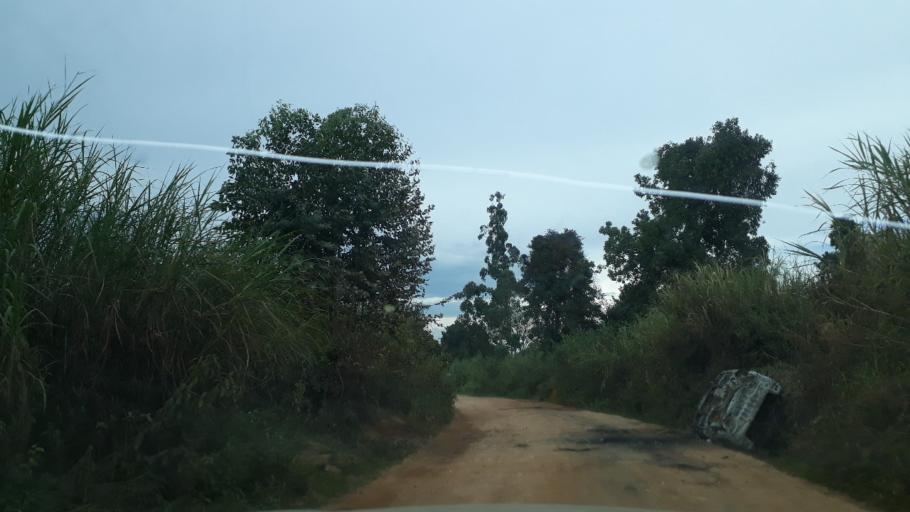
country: CD
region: Eastern Province
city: Bunia
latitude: 1.9298
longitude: 30.5156
